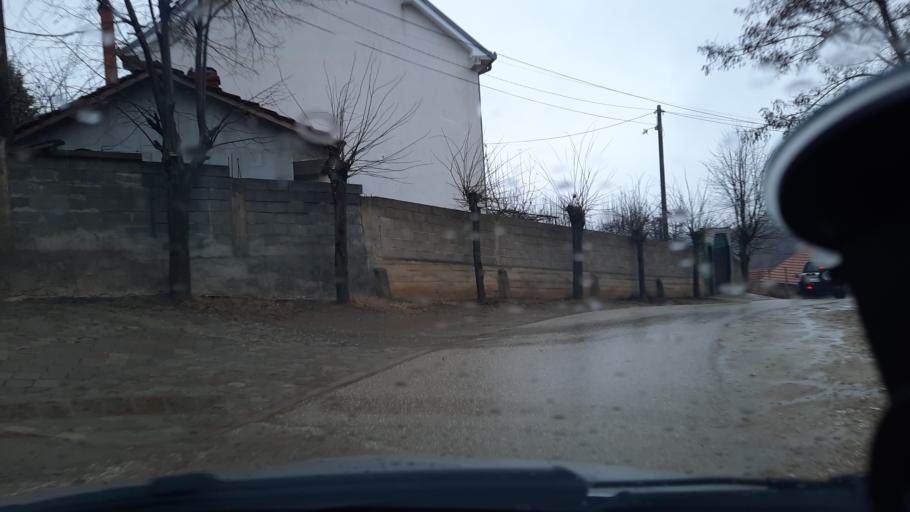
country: MK
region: Opstina Lipkovo
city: Otlja
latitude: 42.1469
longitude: 21.5778
